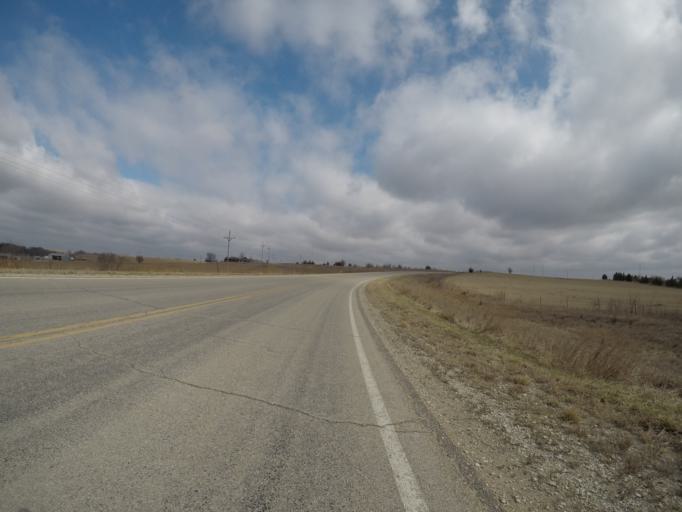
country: US
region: Kansas
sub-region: Pottawatomie County
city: Westmoreland
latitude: 39.3902
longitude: -96.4264
